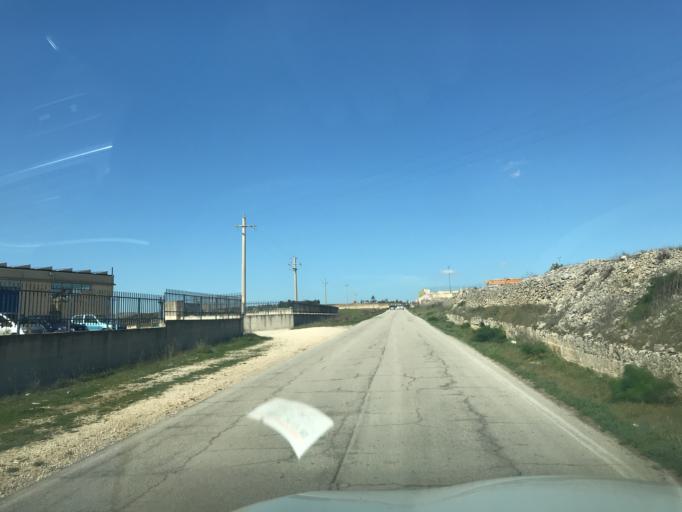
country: IT
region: Apulia
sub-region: Provincia di Bari
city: Gravina in Puglia
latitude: 40.8424
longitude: 16.4261
